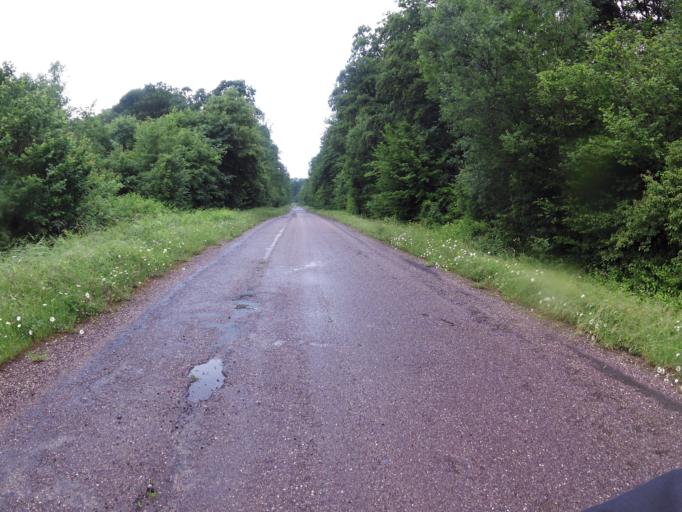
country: FR
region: Champagne-Ardenne
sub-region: Departement de la Marne
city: Sermaize-les-Bains
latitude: 48.7645
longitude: 4.9443
